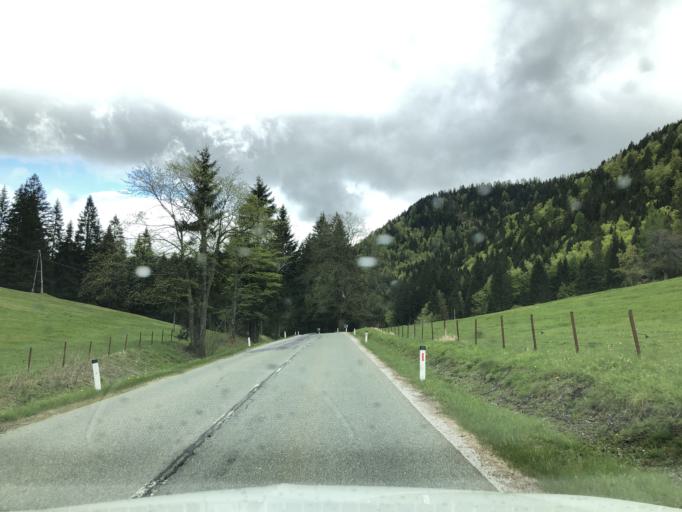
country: AT
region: Carinthia
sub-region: Politischer Bezirk Villach Land
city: Arnoldstein
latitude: 46.5128
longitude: 13.7506
